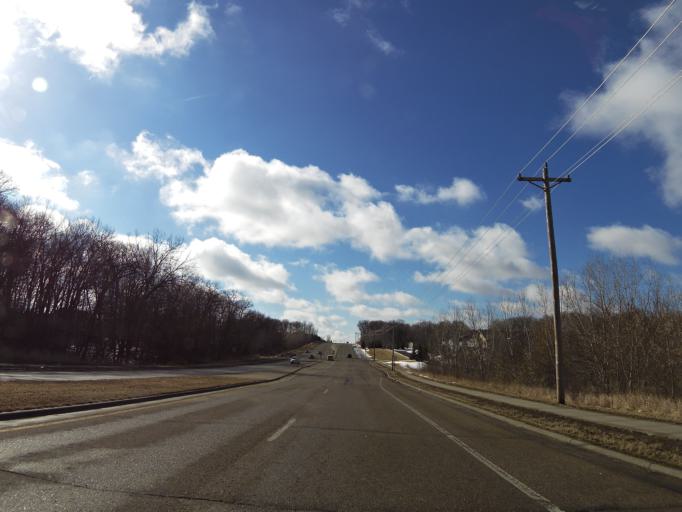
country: US
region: Minnesota
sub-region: Scott County
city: Prior Lake
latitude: 44.7332
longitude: -93.4397
